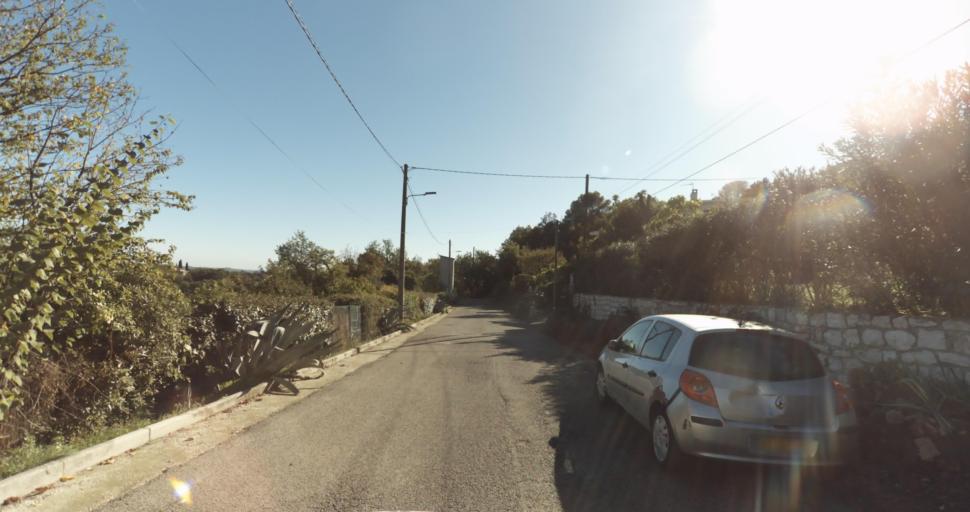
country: FR
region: Provence-Alpes-Cote d'Azur
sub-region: Departement des Alpes-Maritimes
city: Vence
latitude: 43.7162
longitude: 7.1130
